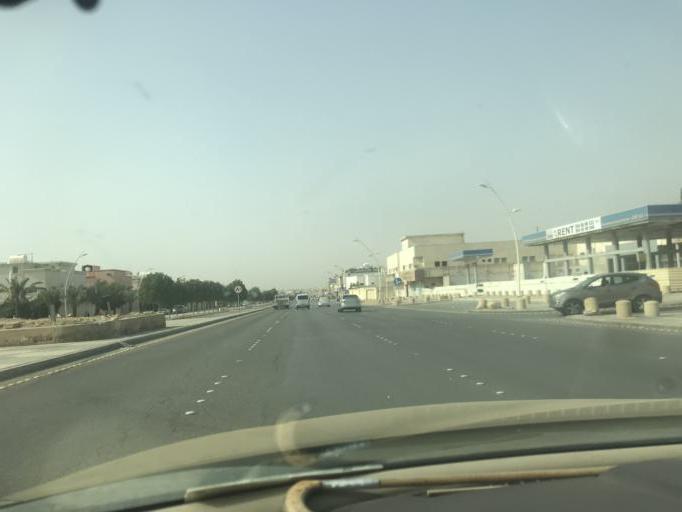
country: SA
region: Ar Riyad
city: Riyadh
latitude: 24.6723
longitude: 46.8039
